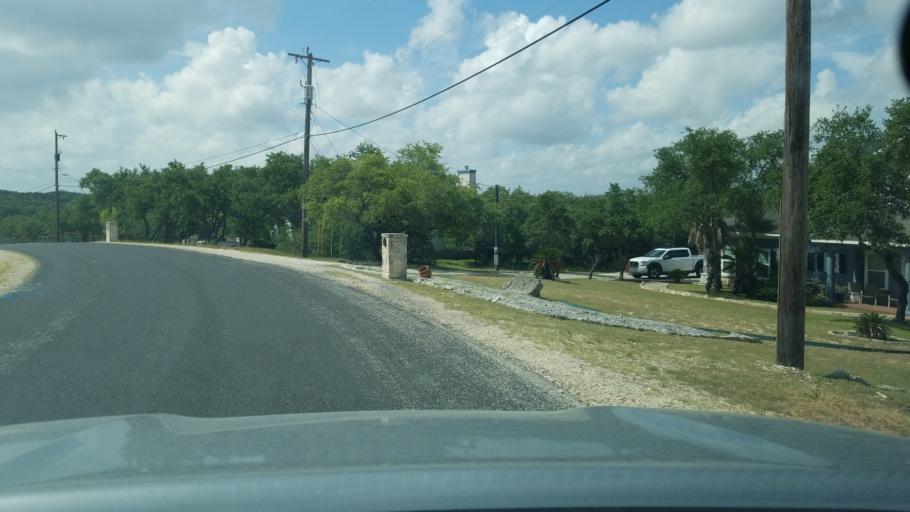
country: US
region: Texas
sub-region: Bexar County
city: Timberwood Park
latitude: 29.6774
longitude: -98.5215
